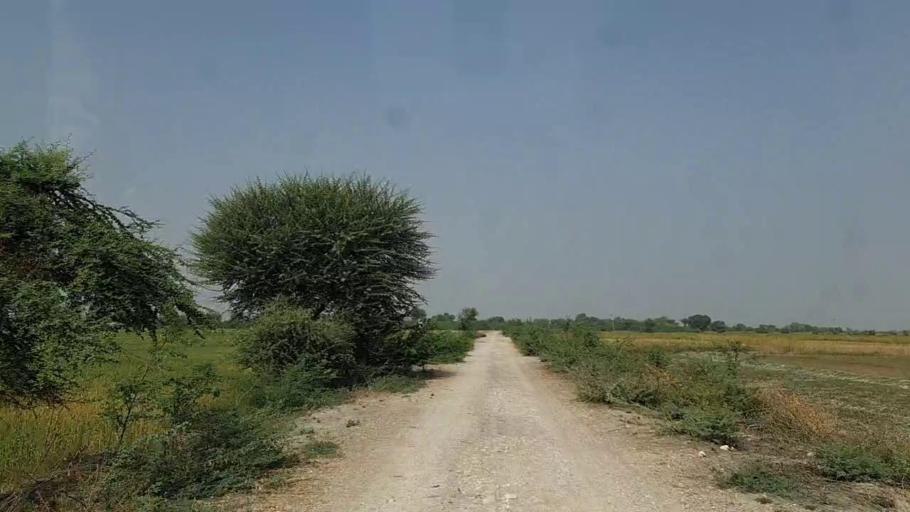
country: PK
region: Sindh
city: Naukot
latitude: 24.8104
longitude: 69.3755
